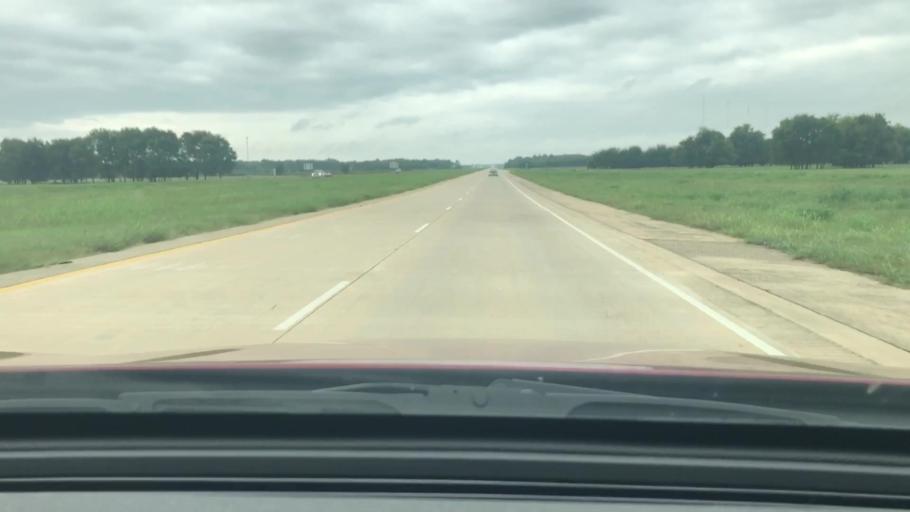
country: US
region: Louisiana
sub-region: Bossier Parish
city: Benton
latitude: 32.6996
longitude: -93.8606
